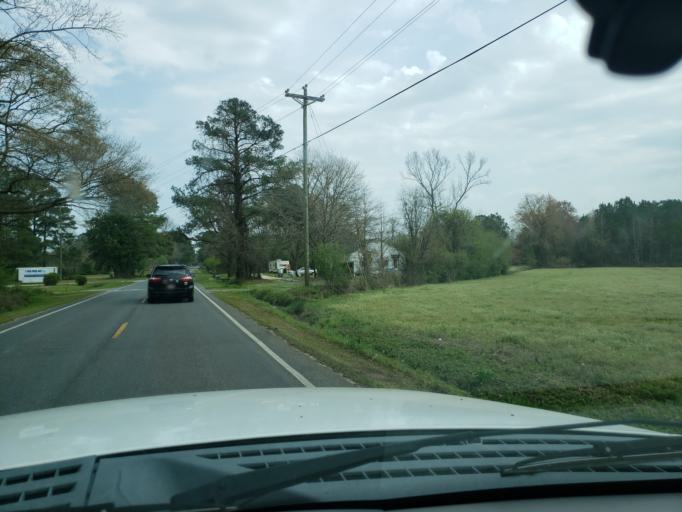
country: US
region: North Carolina
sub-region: Duplin County
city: Beulaville
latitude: 34.7760
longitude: -77.8196
